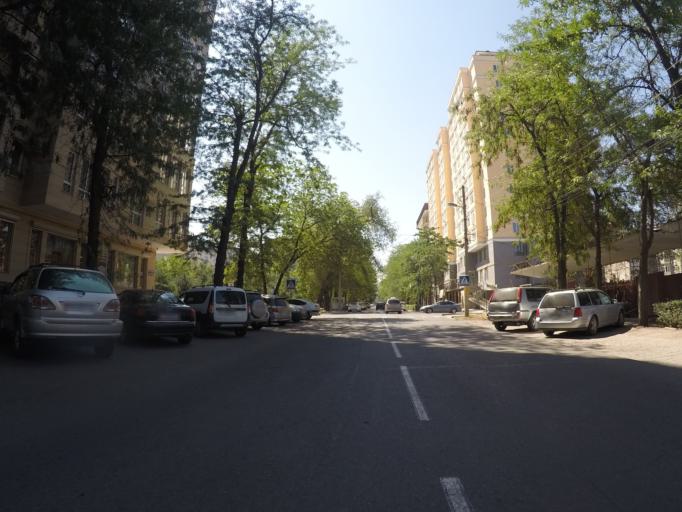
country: KG
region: Chuy
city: Bishkek
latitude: 42.8795
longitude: 74.5920
